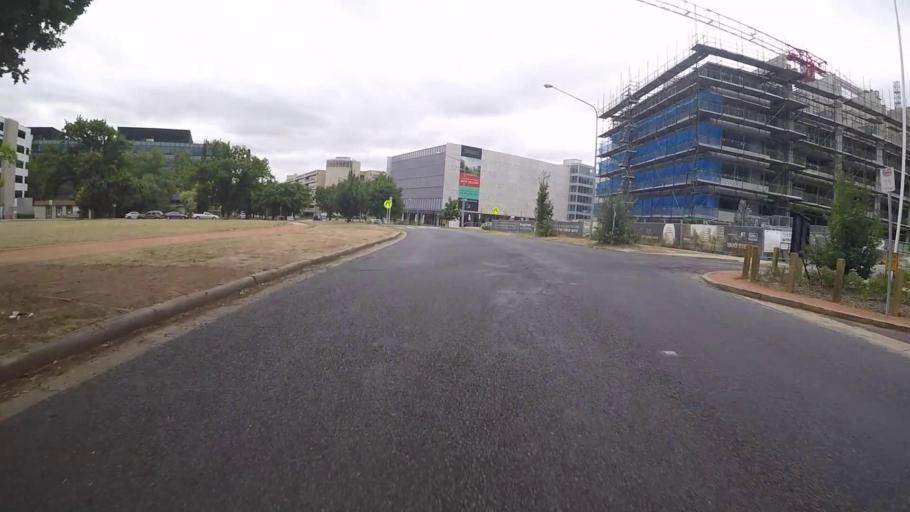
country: AU
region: Australian Capital Territory
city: Forrest
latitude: -35.3072
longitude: 149.1354
